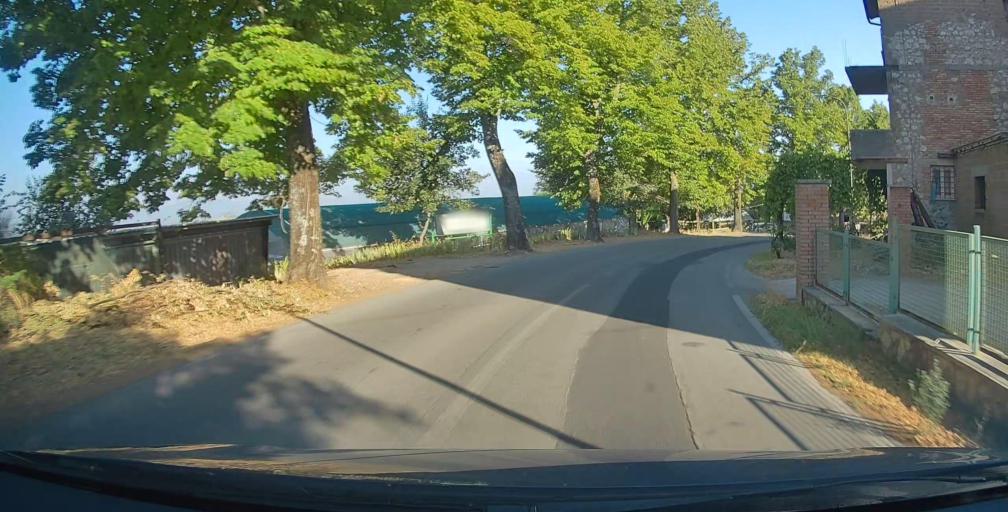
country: IT
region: Umbria
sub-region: Provincia di Terni
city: Calvi dell'Umbria
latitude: 42.3919
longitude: 12.5654
